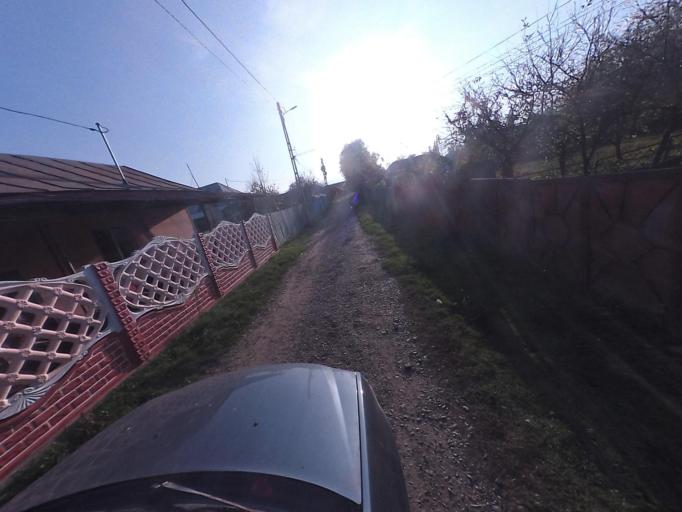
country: RO
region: Vaslui
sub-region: Comuna Bacesti
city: Bacesti
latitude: 46.8228
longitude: 27.2448
